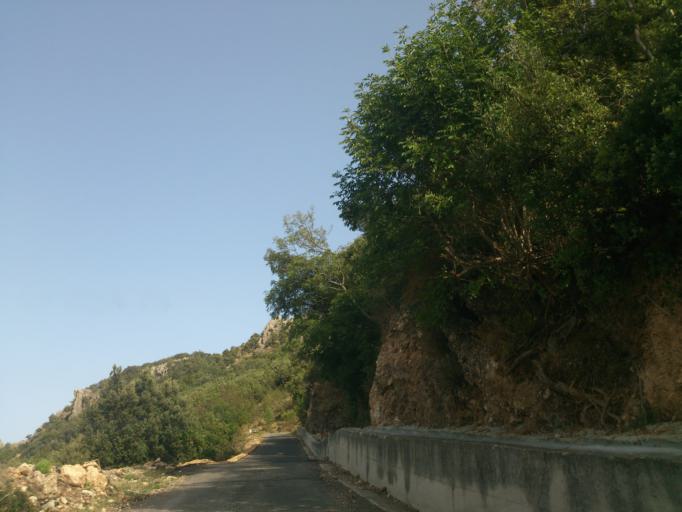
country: IT
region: Calabria
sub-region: Provincia di Reggio Calabria
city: Pazzano
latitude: 38.4658
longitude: 16.4327
